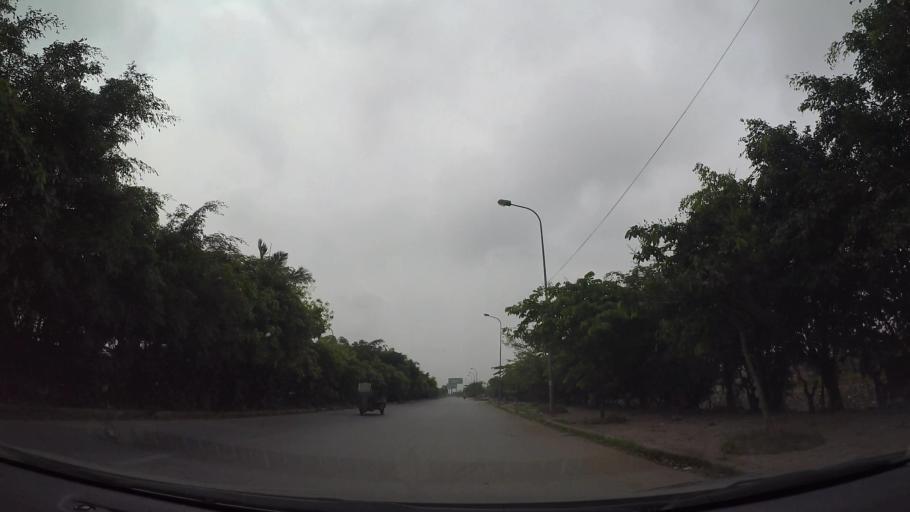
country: VN
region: Ha Noi
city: Trau Quy
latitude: 21.0347
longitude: 105.9337
